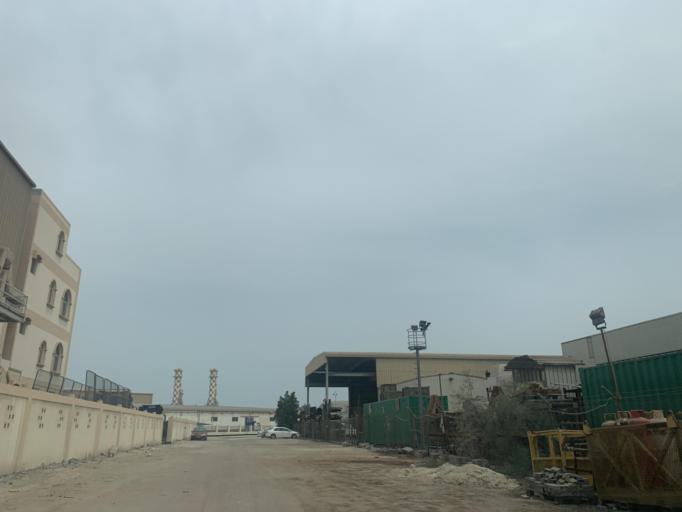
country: BH
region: Muharraq
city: Al Hadd
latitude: 26.2162
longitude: 50.6530
